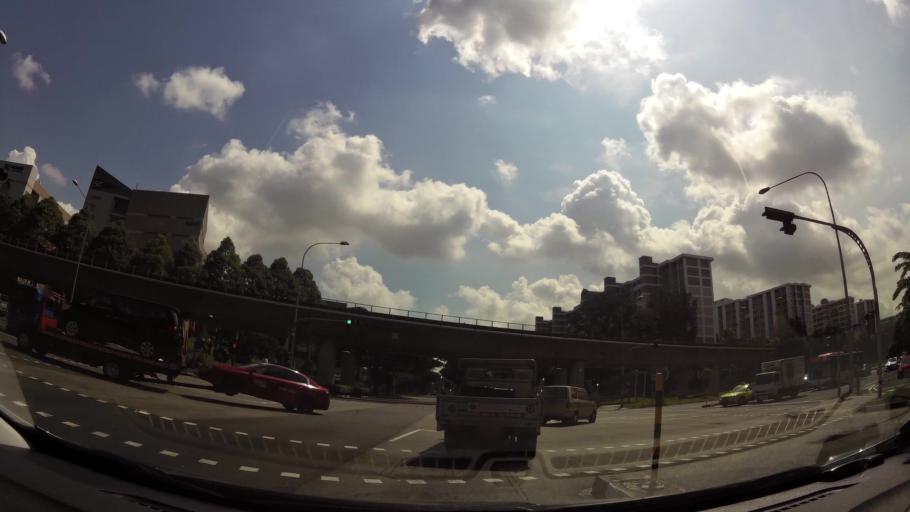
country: SG
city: Singapore
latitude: 1.3768
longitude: 103.8476
